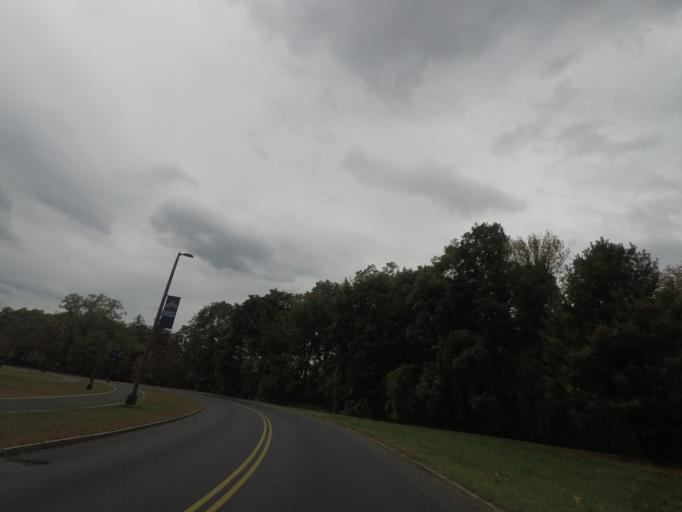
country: US
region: New York
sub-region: Albany County
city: McKownville
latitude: 42.6809
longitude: -73.8302
